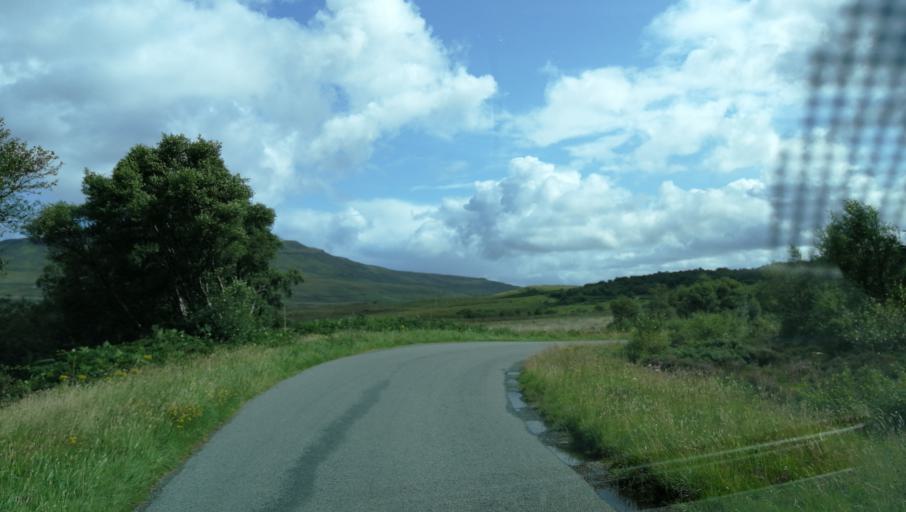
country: GB
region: Scotland
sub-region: Highland
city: Portree
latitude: 57.3849
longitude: -6.1870
